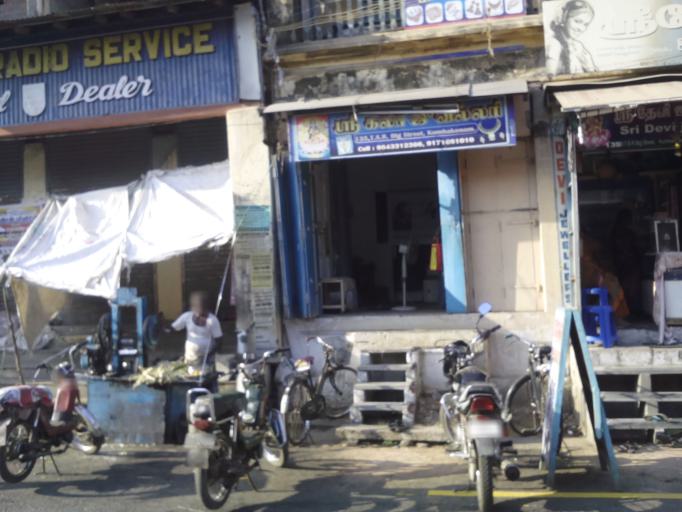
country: IN
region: Tamil Nadu
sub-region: Thanjavur
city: Kumbakonam
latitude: 10.9608
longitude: 79.3755
